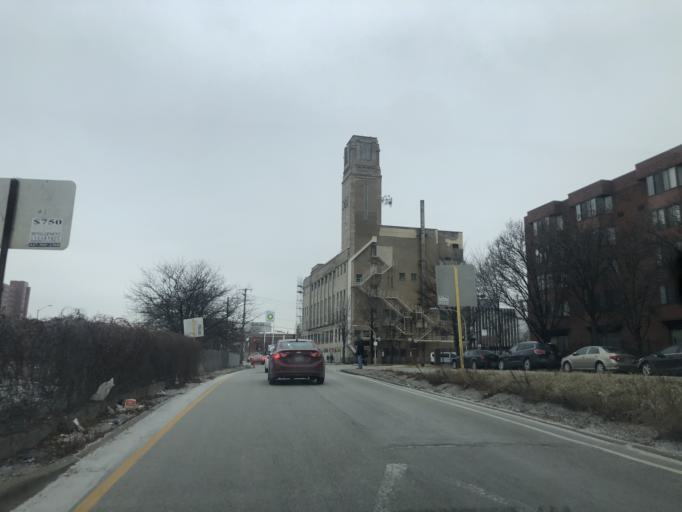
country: US
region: Illinois
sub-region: Cook County
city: Chicago
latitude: 41.8763
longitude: -87.6647
